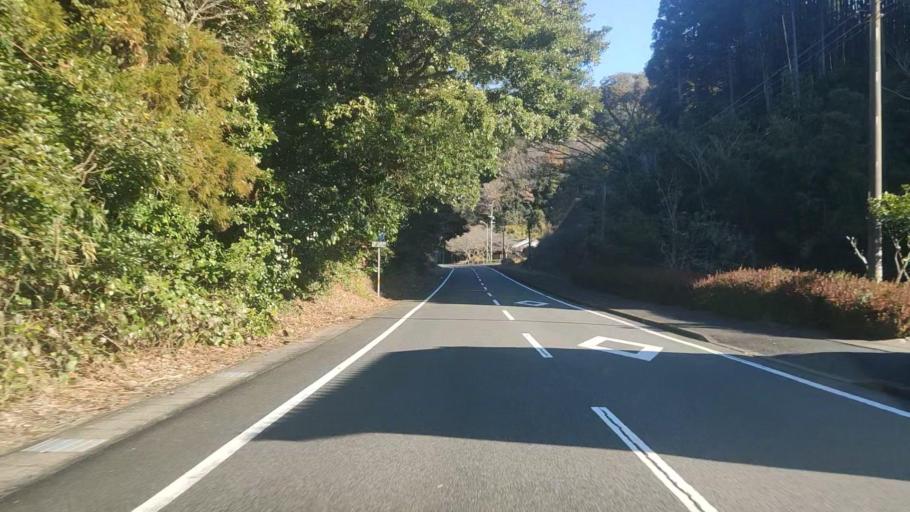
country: JP
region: Miyazaki
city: Nobeoka
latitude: 32.6893
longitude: 131.8087
